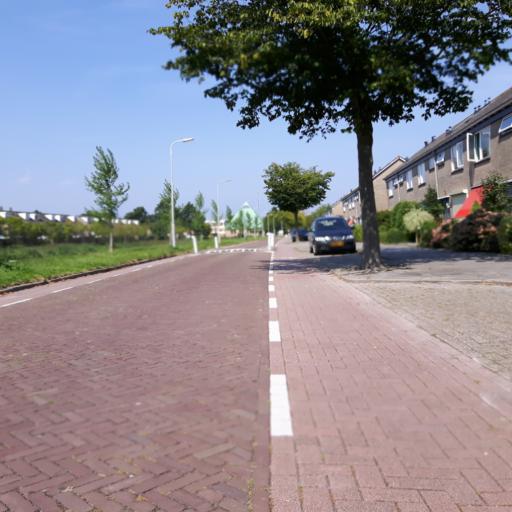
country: NL
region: Zeeland
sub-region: Gemeente Goes
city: Goes
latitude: 51.4916
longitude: 3.8999
